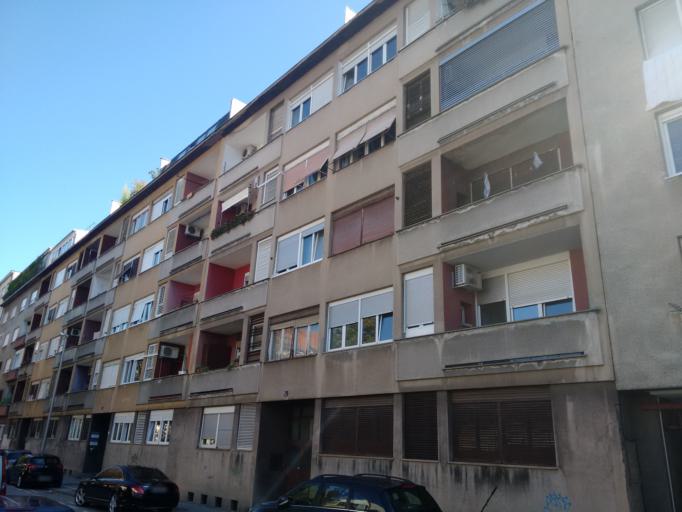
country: HR
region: Grad Zagreb
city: Zagreb - Centar
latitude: 45.8074
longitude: 15.9939
